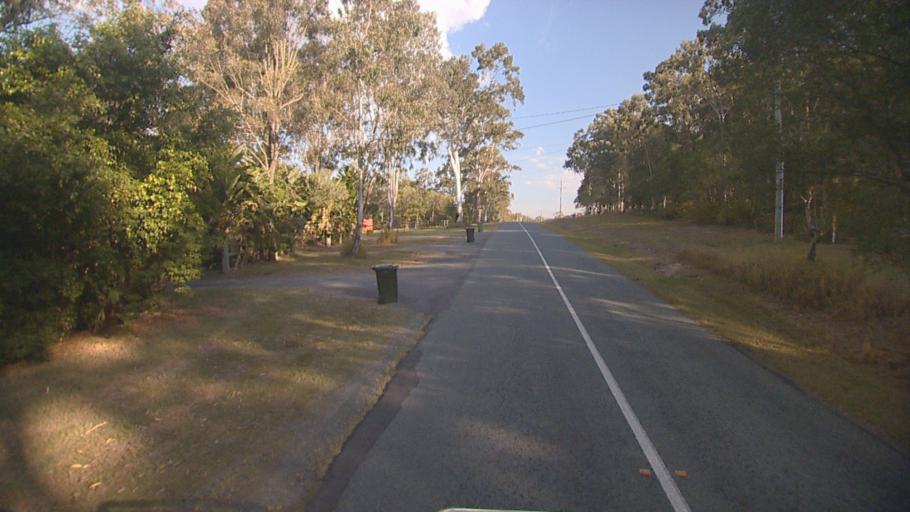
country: AU
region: Queensland
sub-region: Gold Coast
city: Ormeau Hills
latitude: -27.8334
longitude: 153.1697
